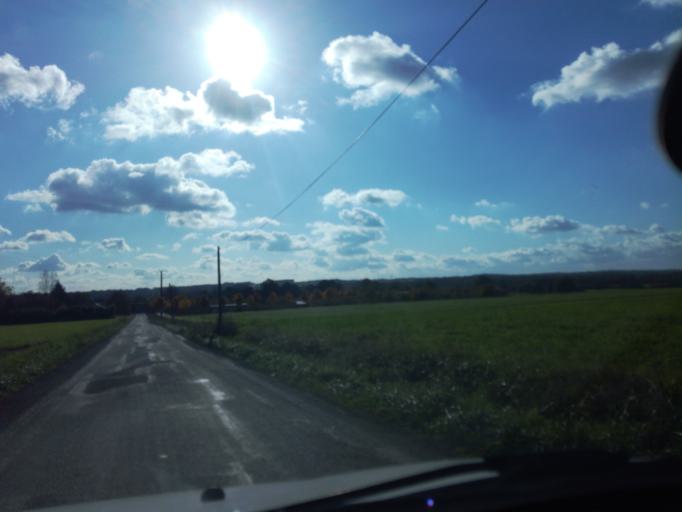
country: FR
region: Brittany
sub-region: Departement d'Ille-et-Vilaine
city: Chavagne
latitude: 48.0566
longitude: -1.7998
